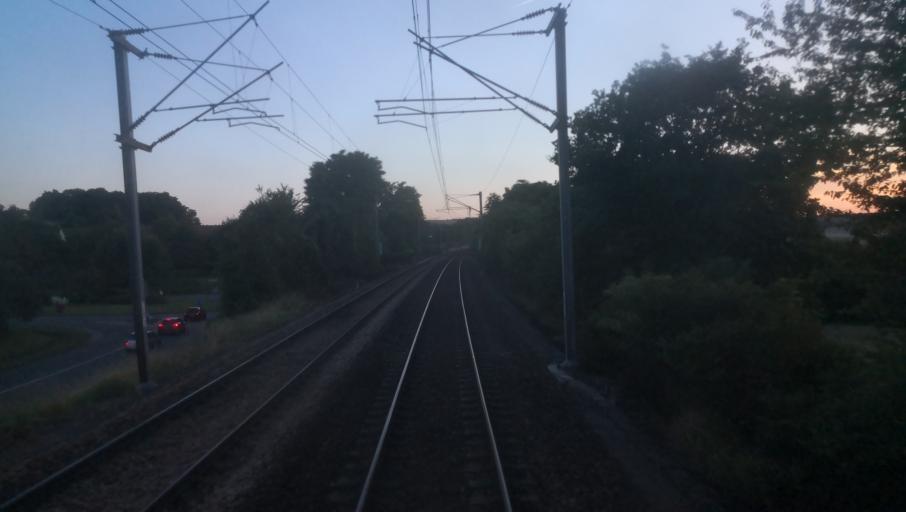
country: FR
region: Ile-de-France
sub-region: Departement des Yvelines
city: Buchelay
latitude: 48.9829
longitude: 1.6638
